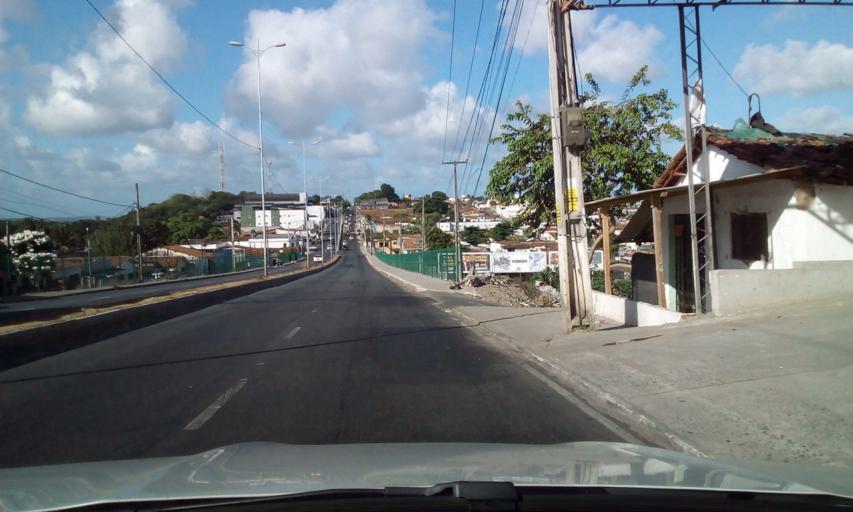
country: BR
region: Paraiba
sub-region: Bayeux
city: Bayeux
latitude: -7.1559
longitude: -34.8959
